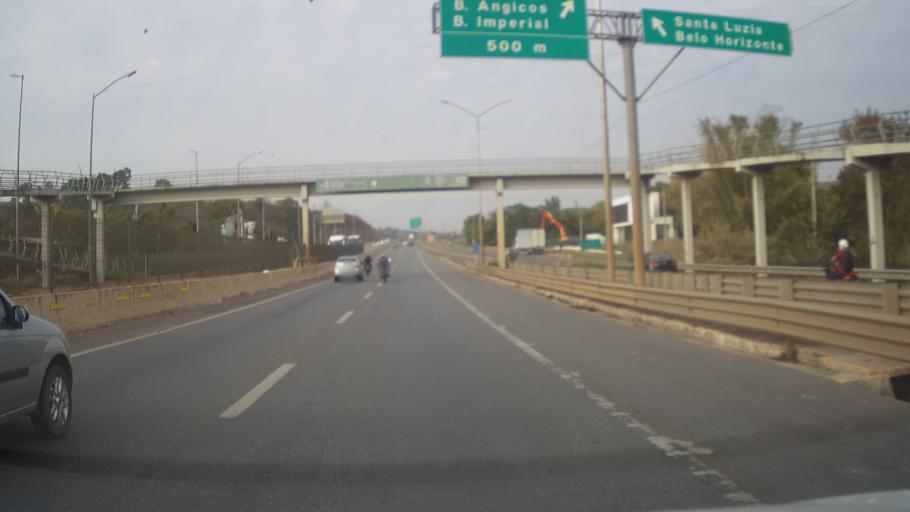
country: BR
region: Minas Gerais
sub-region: Vespasiano
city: Vespasiano
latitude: -19.7136
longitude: -43.9265
